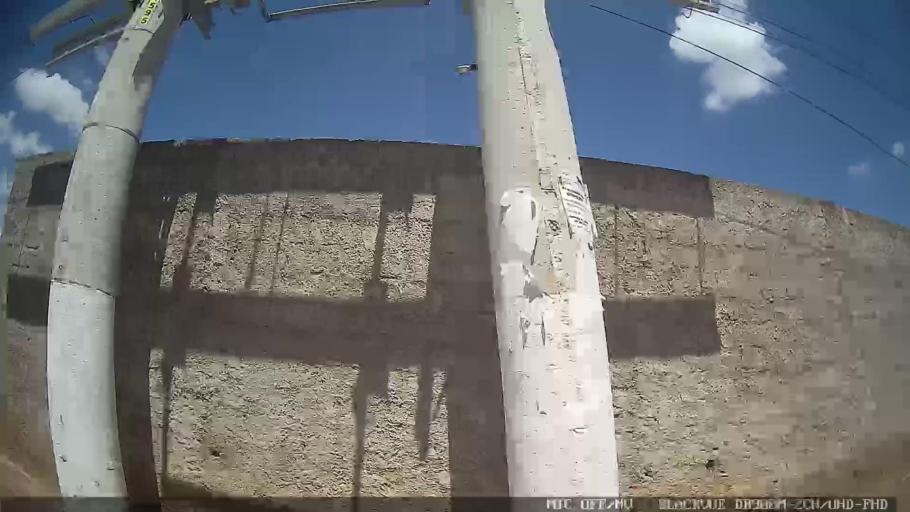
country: BR
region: Sao Paulo
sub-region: Atibaia
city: Atibaia
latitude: -23.1306
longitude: -46.6000
